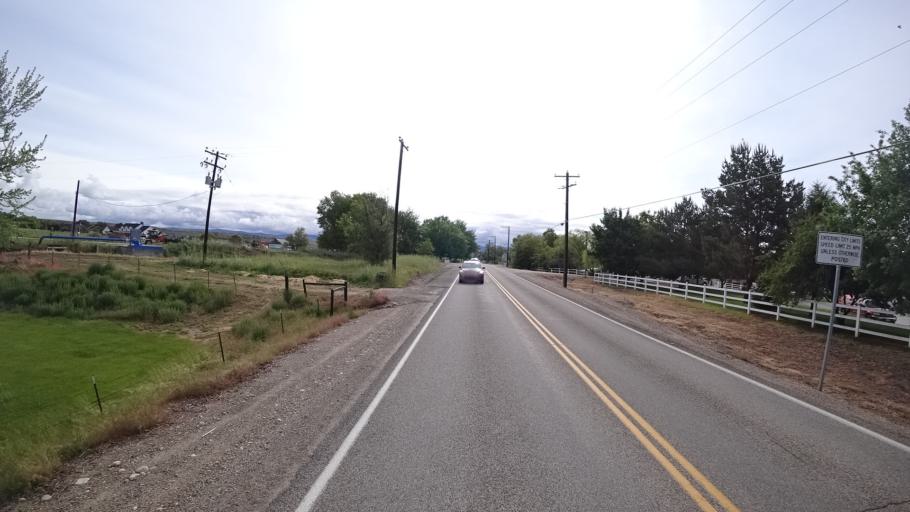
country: US
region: Idaho
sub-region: Ada County
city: Eagle
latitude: 43.7208
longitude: -116.3607
